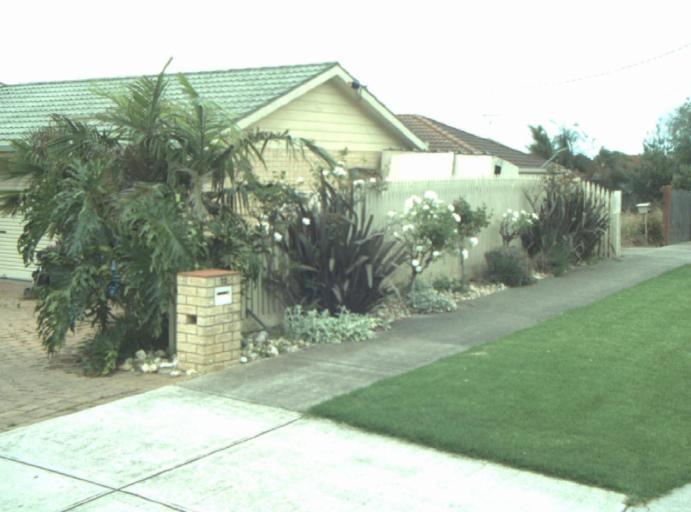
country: AU
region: Victoria
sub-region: Greater Geelong
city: Breakwater
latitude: -38.2073
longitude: 144.3451
